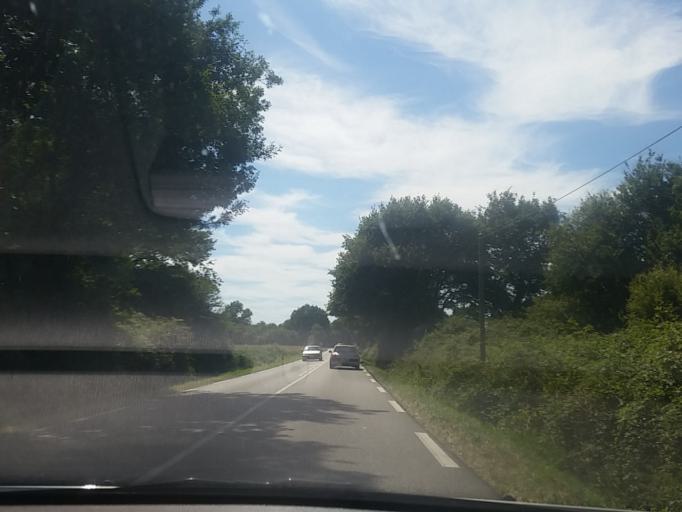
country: FR
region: Pays de la Loire
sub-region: Departement de la Loire-Atlantique
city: Vue
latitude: 47.1937
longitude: -1.9253
